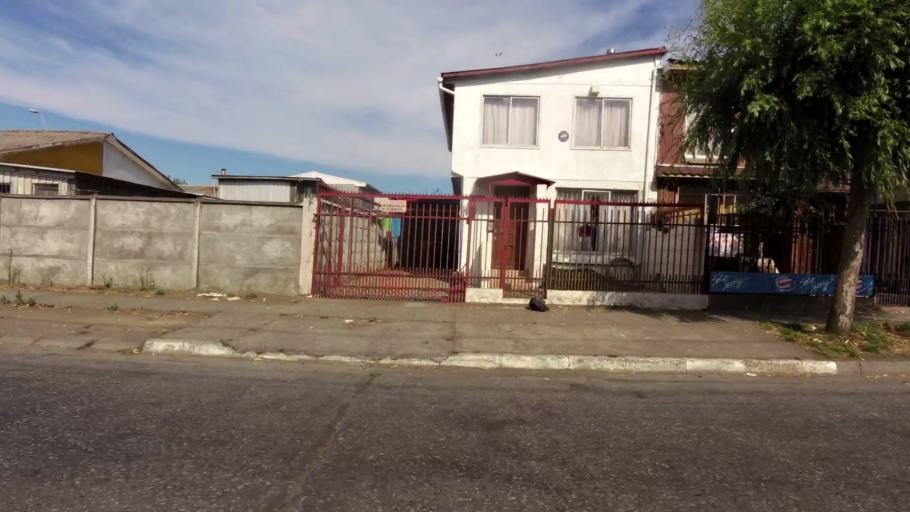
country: CL
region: Biobio
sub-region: Provincia de Concepcion
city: Talcahuano
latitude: -36.7864
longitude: -73.1017
